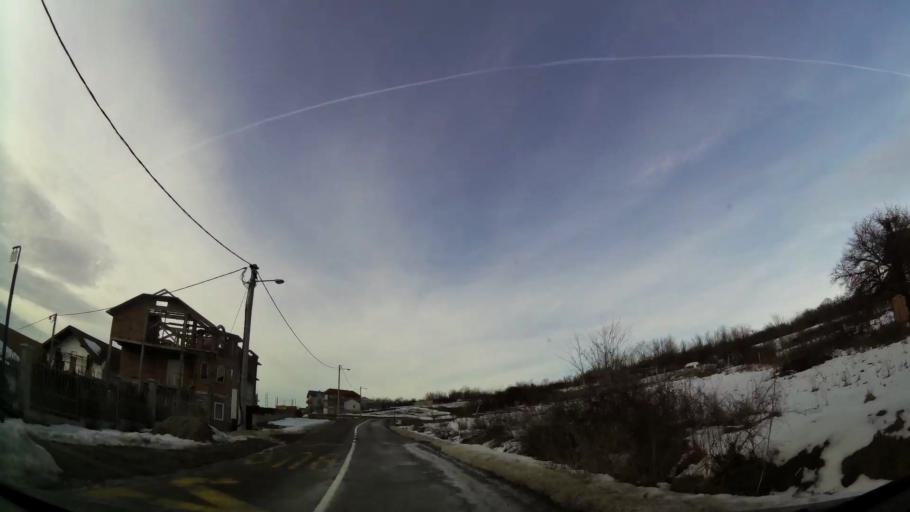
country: RS
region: Central Serbia
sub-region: Belgrade
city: Zvezdara
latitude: 44.7249
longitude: 20.5079
